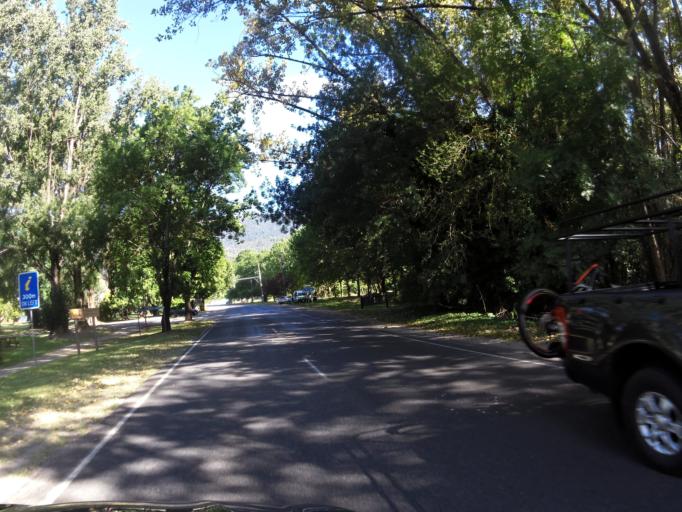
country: AU
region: Victoria
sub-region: Alpine
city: Mount Beauty
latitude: -36.7401
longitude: 147.1630
